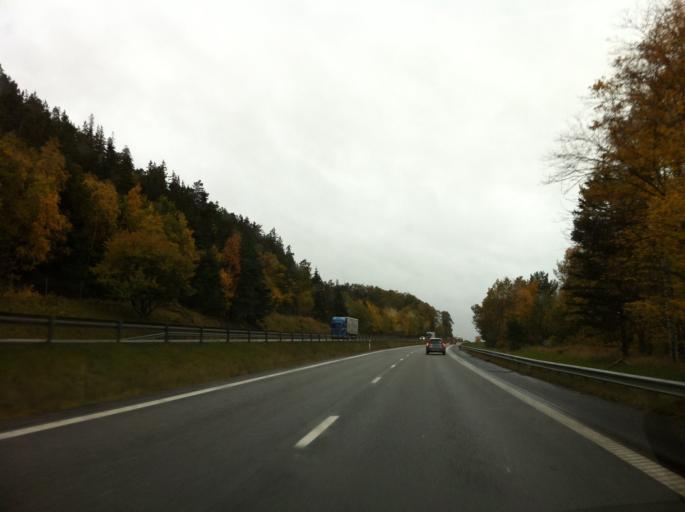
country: SE
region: Joenkoeping
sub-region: Jonkopings Kommun
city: Kaxholmen
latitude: 57.8854
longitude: 14.2829
